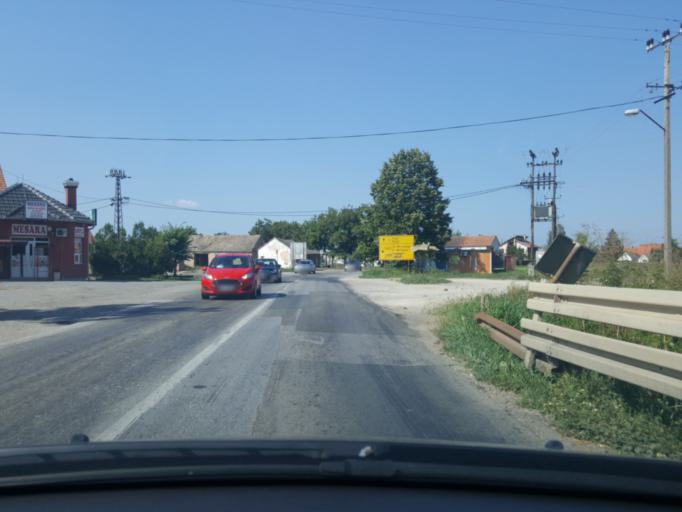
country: RS
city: Jarak
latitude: 44.9118
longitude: 19.7649
